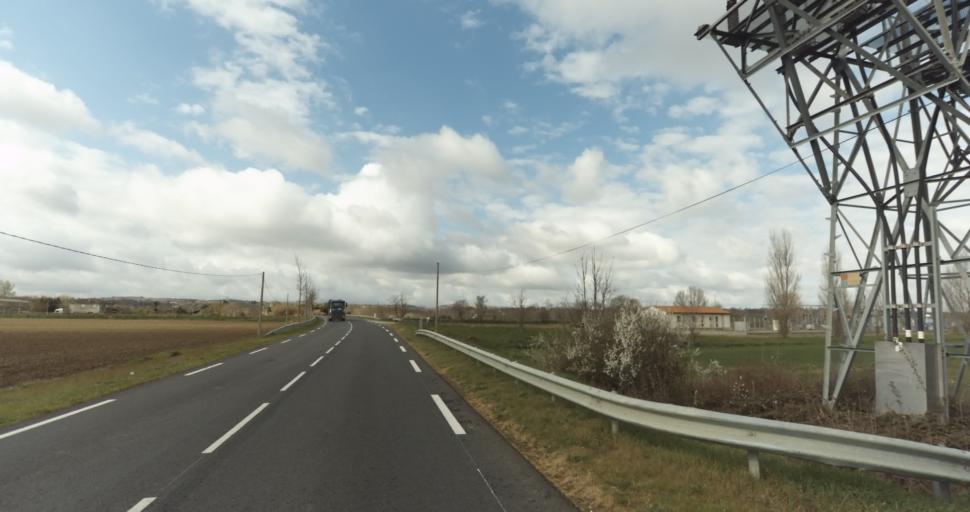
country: FR
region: Midi-Pyrenees
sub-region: Departement de la Haute-Garonne
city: Auterive
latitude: 43.3471
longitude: 1.4470
